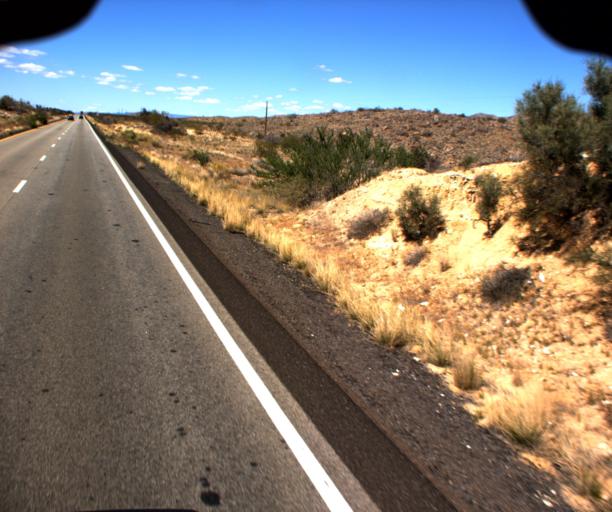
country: US
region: Arizona
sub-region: Mohave County
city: Kingman
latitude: 34.9716
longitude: -113.6694
